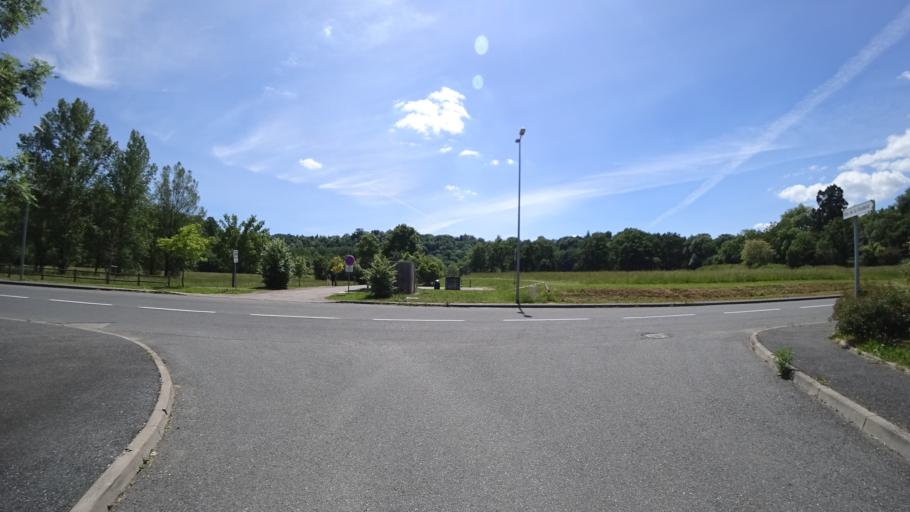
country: FR
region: Midi-Pyrenees
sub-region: Departement de l'Aveyron
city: Rodez
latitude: 44.3581
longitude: 2.5944
